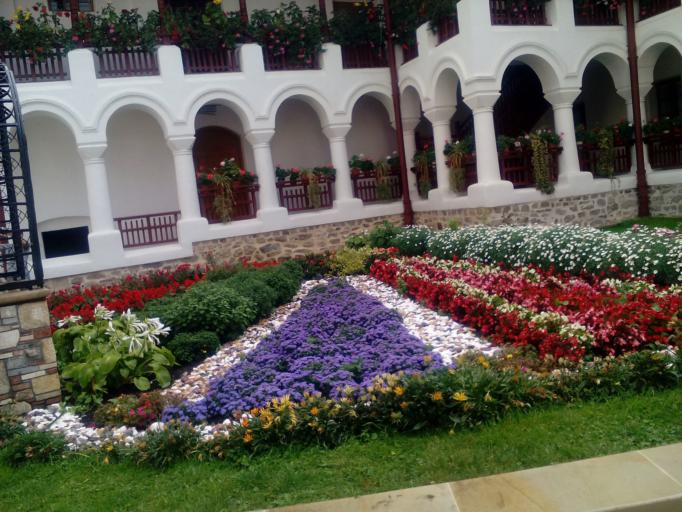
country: RO
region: Neamt
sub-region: Comuna Agapia
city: Filioara
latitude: 47.1702
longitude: 26.2352
